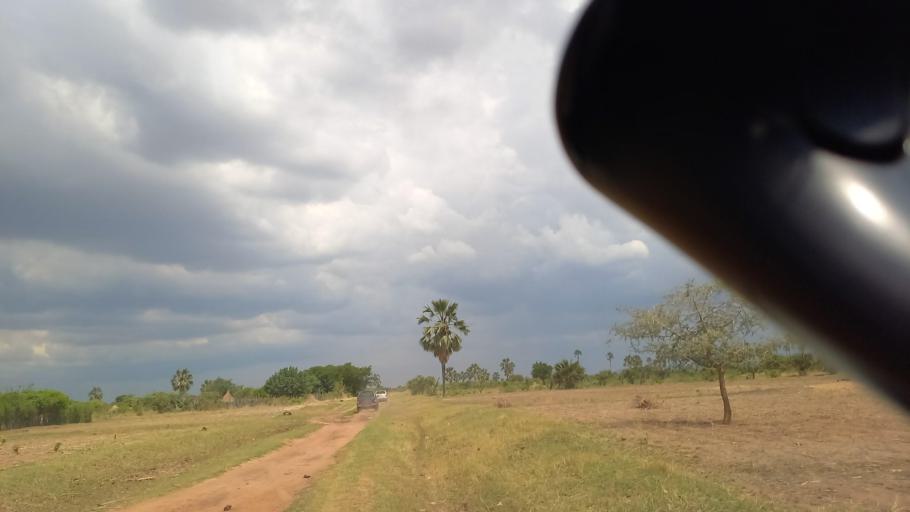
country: ZM
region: Lusaka
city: Kafue
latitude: -15.8319
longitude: 28.0663
